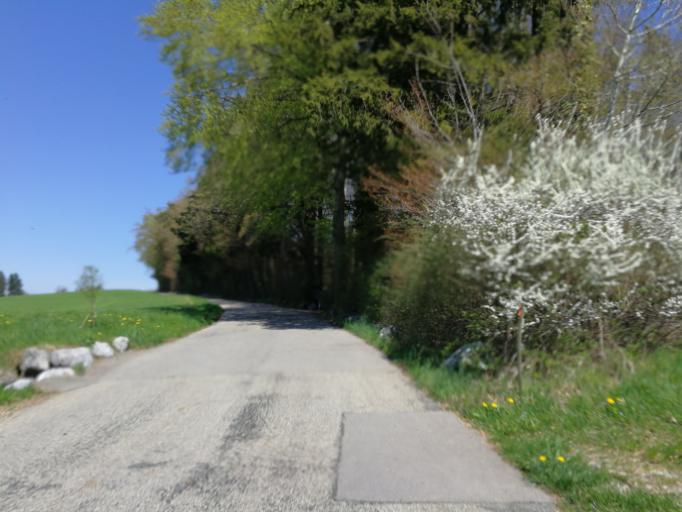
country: CH
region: Zurich
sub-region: Bezirk Meilen
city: Herrliberg
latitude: 47.3022
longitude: 8.6413
